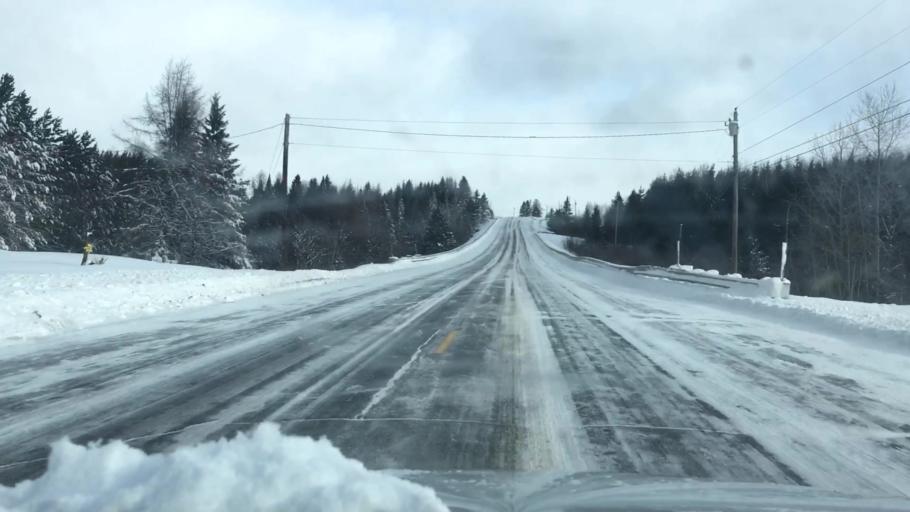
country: US
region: Maine
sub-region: Aroostook County
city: Van Buren
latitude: 47.0938
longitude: -67.9796
